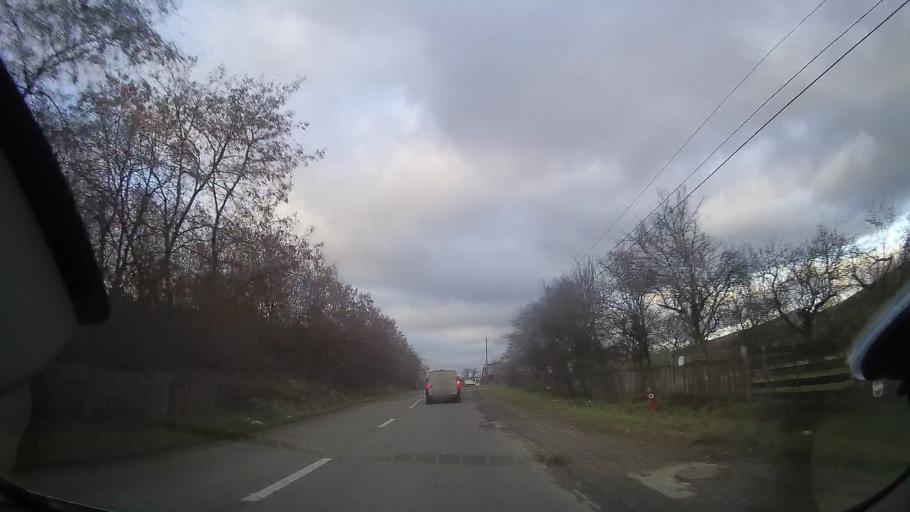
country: RO
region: Cluj
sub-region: Comuna Sancraiu
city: Sancraiu
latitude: 46.8010
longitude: 22.9949
